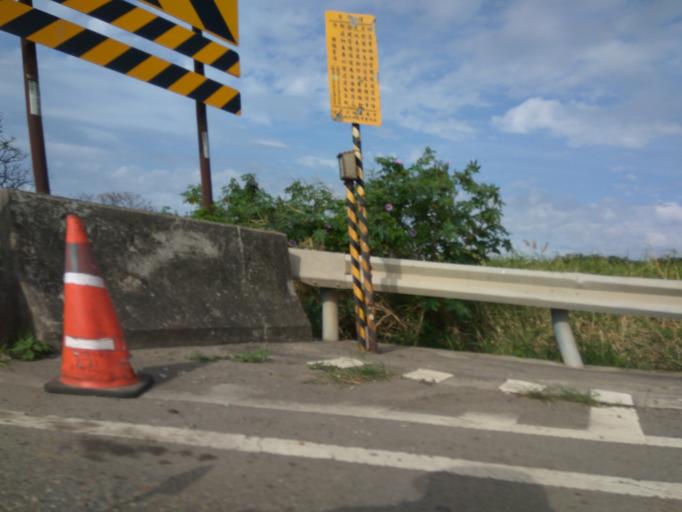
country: TW
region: Taiwan
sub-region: Hsinchu
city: Zhubei
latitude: 24.9660
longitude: 121.0165
